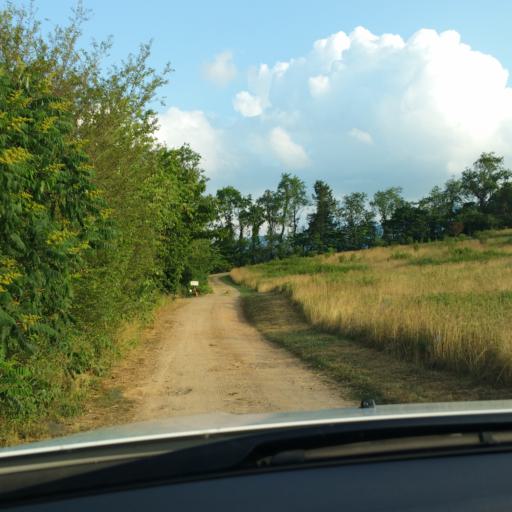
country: US
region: North Carolina
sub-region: Buncombe County
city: Bent Creek
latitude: 35.5127
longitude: -82.6856
